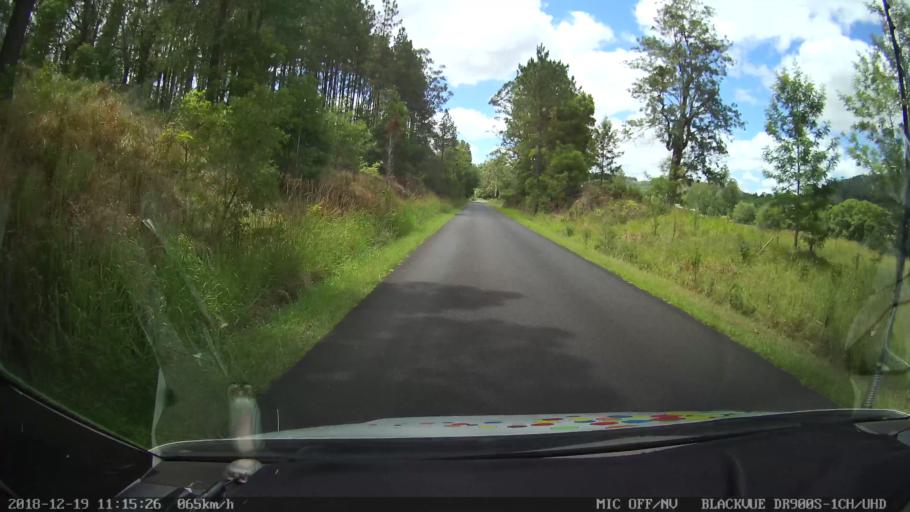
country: AU
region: New South Wales
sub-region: Lismore Municipality
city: Nimbin
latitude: -28.6679
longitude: 153.2780
